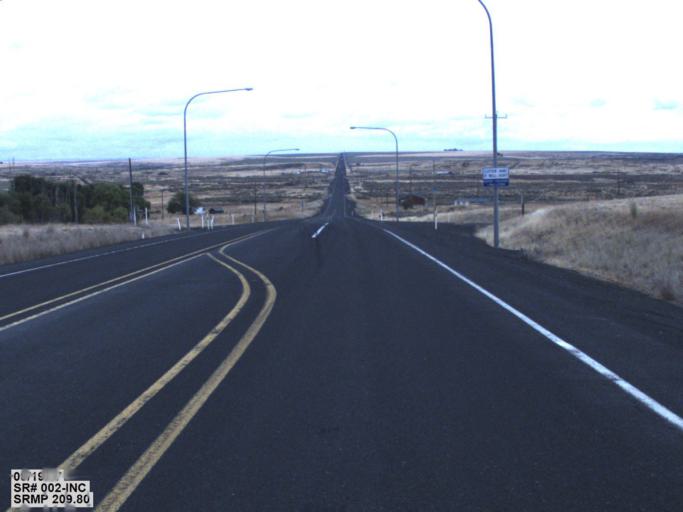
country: US
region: Washington
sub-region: Okanogan County
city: Coulee Dam
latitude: 47.7053
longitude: -118.9405
